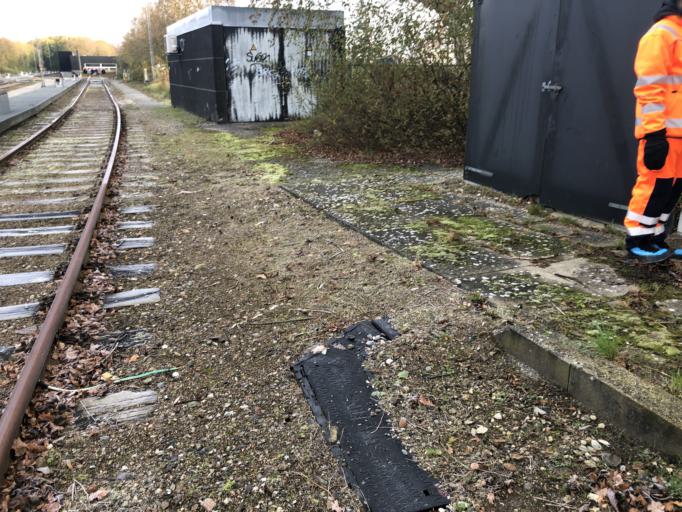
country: DK
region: Zealand
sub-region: Guldborgsund Kommune
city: Nykobing Falster
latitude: 54.7761
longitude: 11.8850
